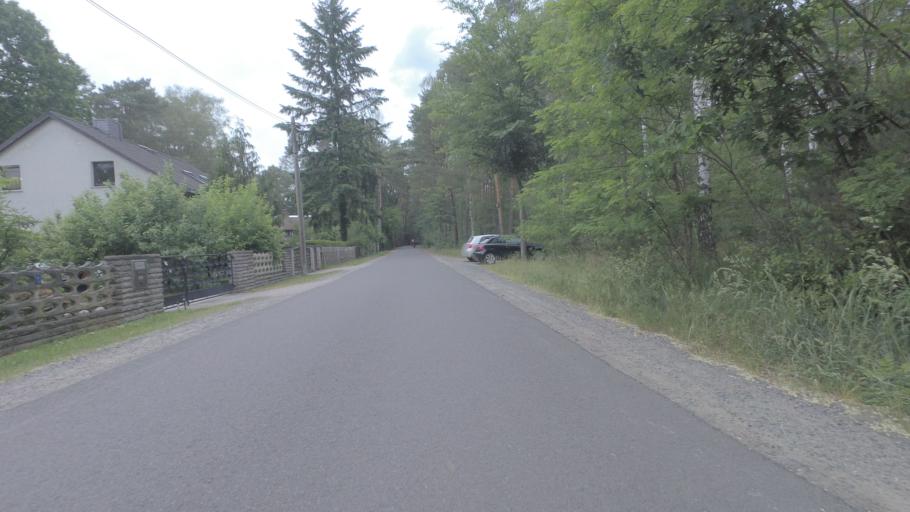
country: DE
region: Brandenburg
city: Bestensee
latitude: 52.2664
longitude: 13.7612
